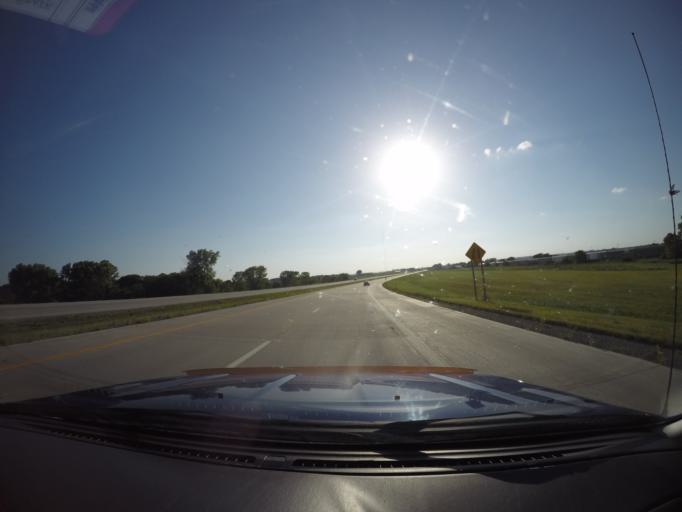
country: US
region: Kansas
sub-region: Shawnee County
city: Topeka
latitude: 39.0906
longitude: -95.7606
